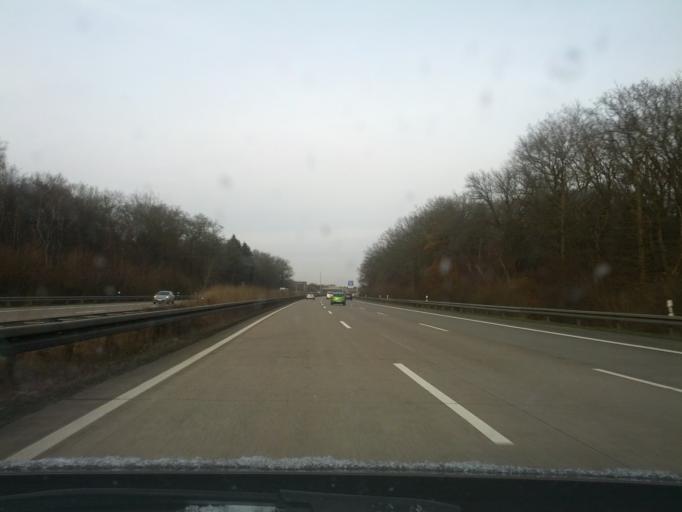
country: DE
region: Lower Saxony
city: Laatzen
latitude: 52.3197
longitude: 9.8650
